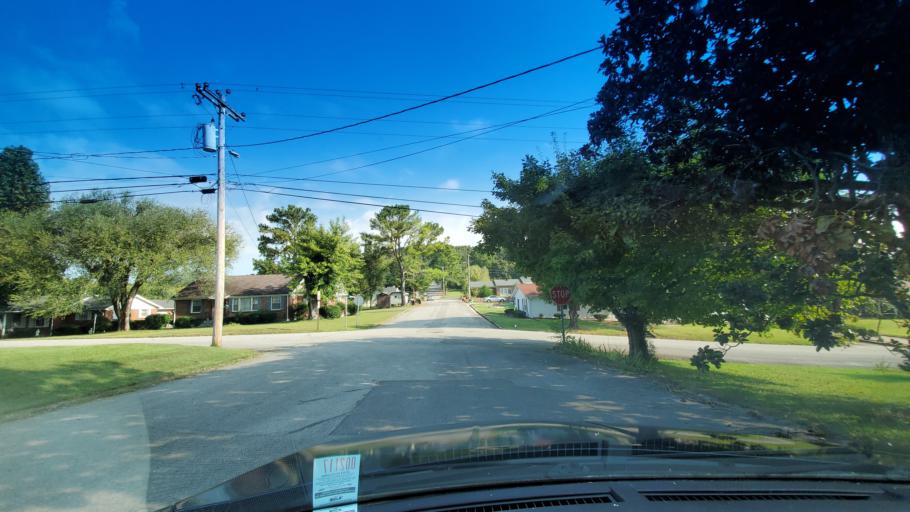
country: US
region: Tennessee
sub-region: Smith County
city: Carthage
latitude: 36.2558
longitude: -85.9411
